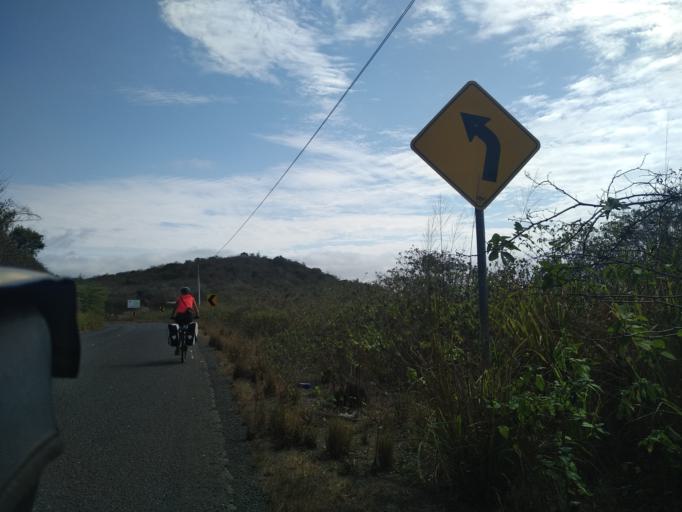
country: EC
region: Manabi
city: Jipijapa
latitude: -1.4469
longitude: -80.7579
